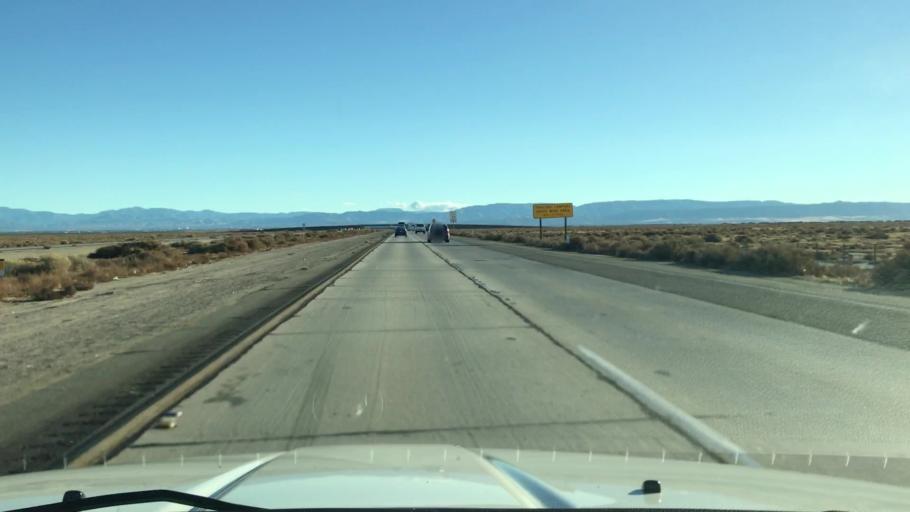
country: US
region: California
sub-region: Kern County
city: Rosamond
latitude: 34.8165
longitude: -118.1708
